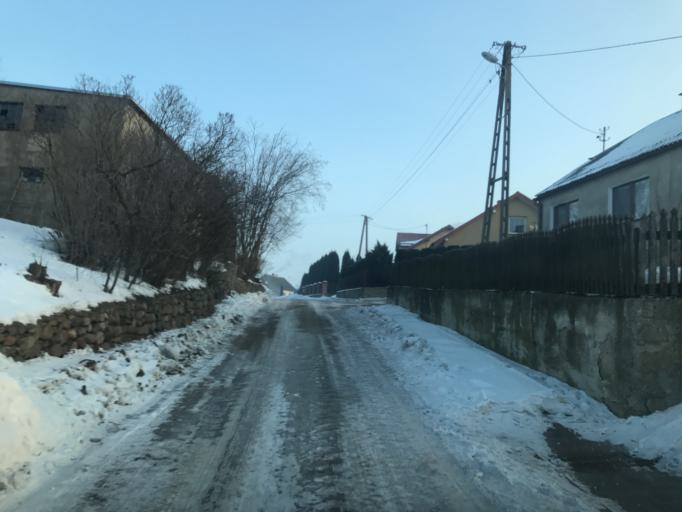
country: PL
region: Warmian-Masurian Voivodeship
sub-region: Powiat dzialdowski
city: Rybno
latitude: 53.4170
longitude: 19.8723
